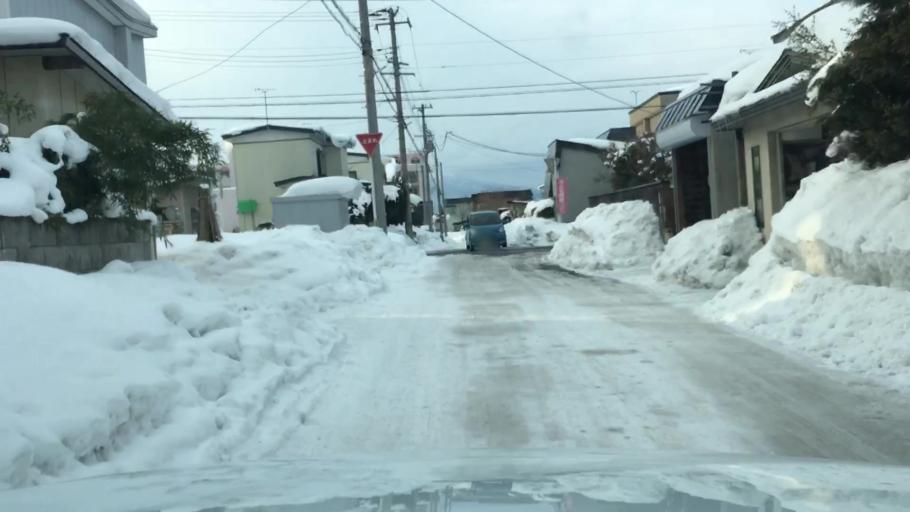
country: JP
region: Aomori
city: Hirosaki
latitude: 40.5797
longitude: 140.4880
